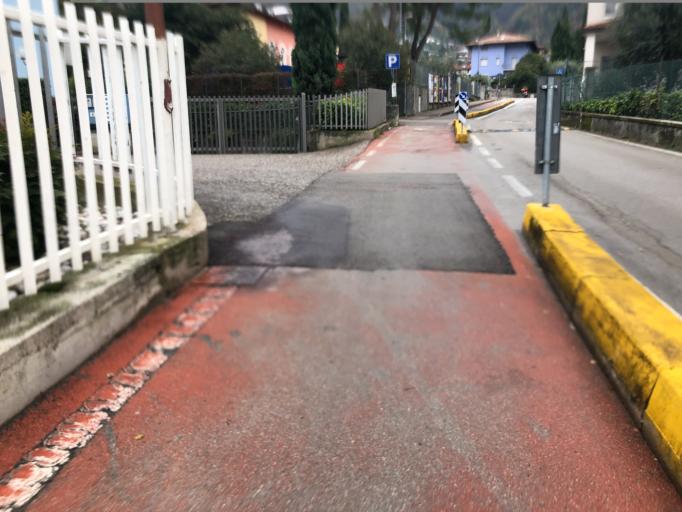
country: IT
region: Trentino-Alto Adige
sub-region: Provincia di Trento
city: Bolognano-Vignole
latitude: 45.9134
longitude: 10.9015
